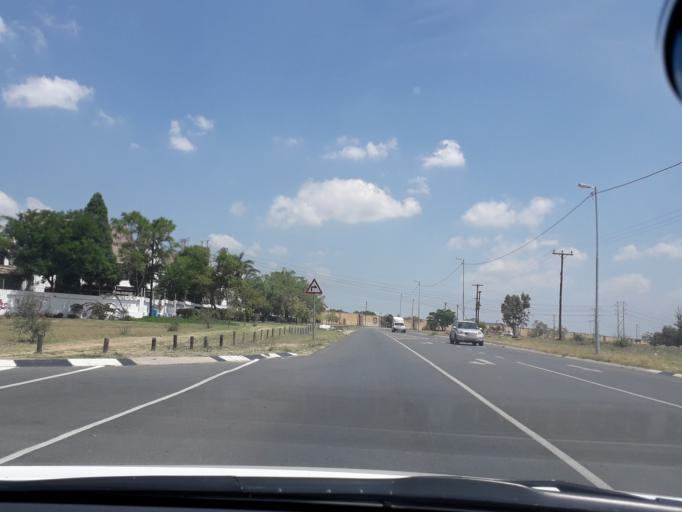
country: ZA
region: Gauteng
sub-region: City of Johannesburg Metropolitan Municipality
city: Midrand
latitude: -26.0126
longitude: 28.0768
